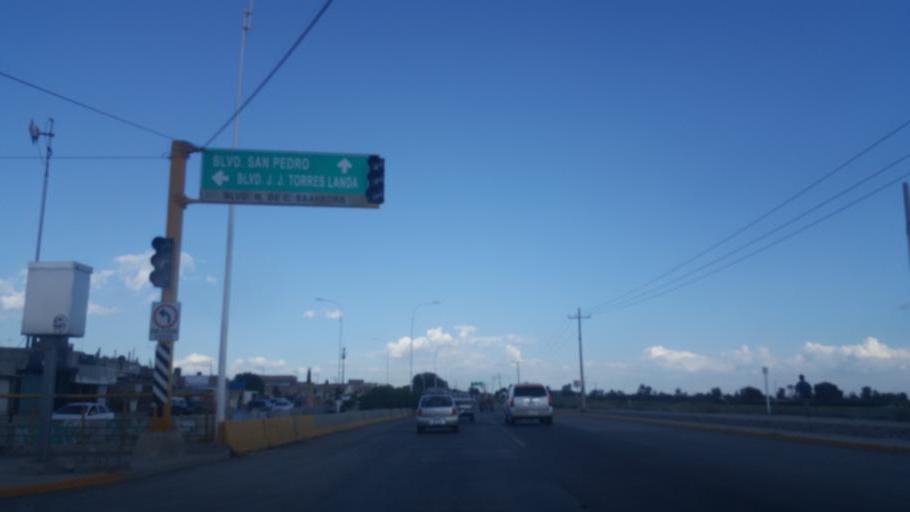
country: MX
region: Guanajuato
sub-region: Leon
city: San Jose de Duran (Los Troncoso)
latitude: 21.0797
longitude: -101.6581
